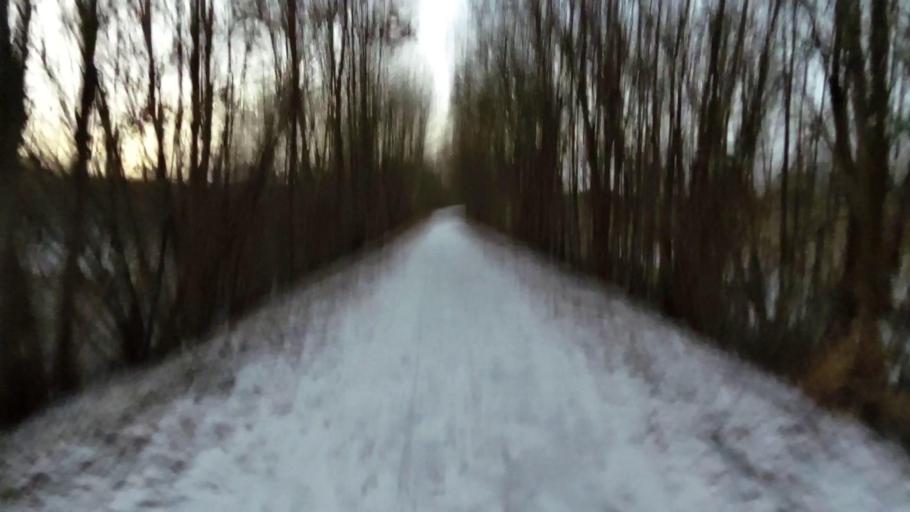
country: PL
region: West Pomeranian Voivodeship
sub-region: Powiat swidwinski
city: Polczyn-Zdroj
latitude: 53.7516
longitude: 16.0591
